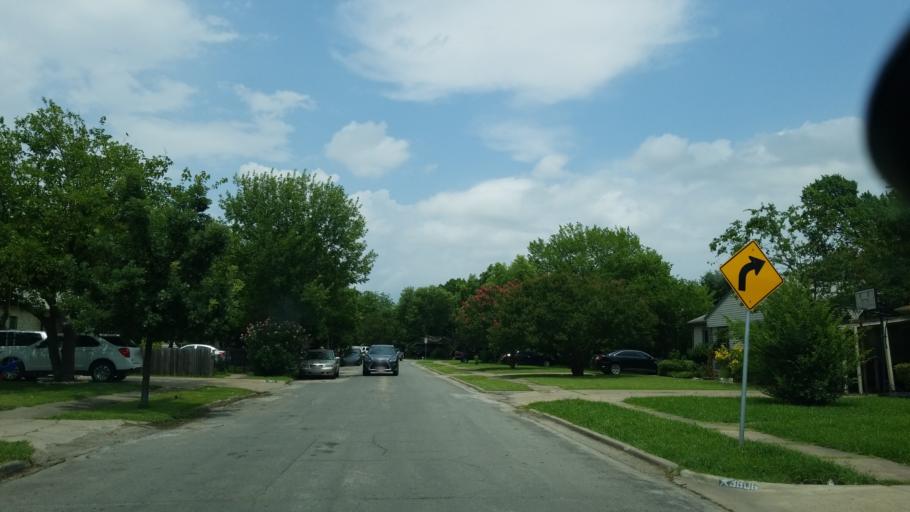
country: US
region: Texas
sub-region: Dallas County
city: Farmers Branch
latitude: 32.8769
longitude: -96.8587
